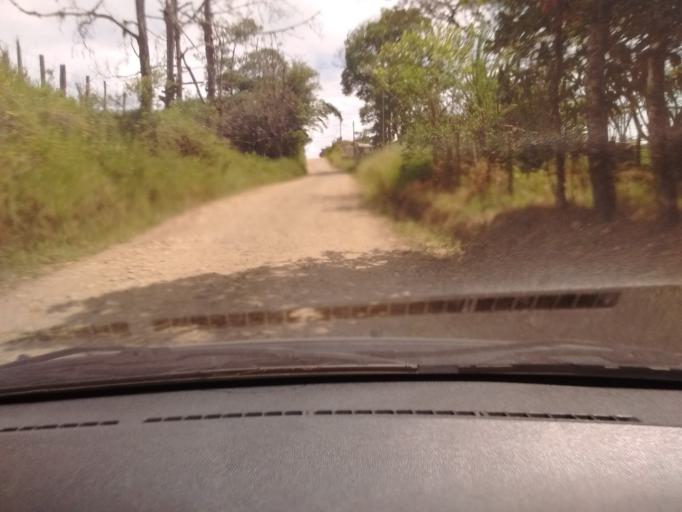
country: CO
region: Cauca
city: El Tambo
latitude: 2.4519
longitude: -76.8241
